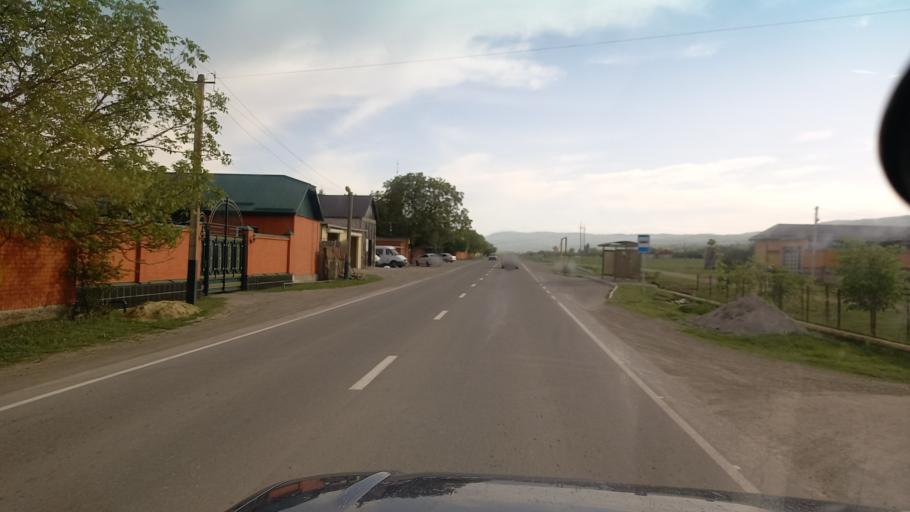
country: RU
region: Ingushetiya
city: Nesterovskaya
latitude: 43.2273
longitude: 45.0357
